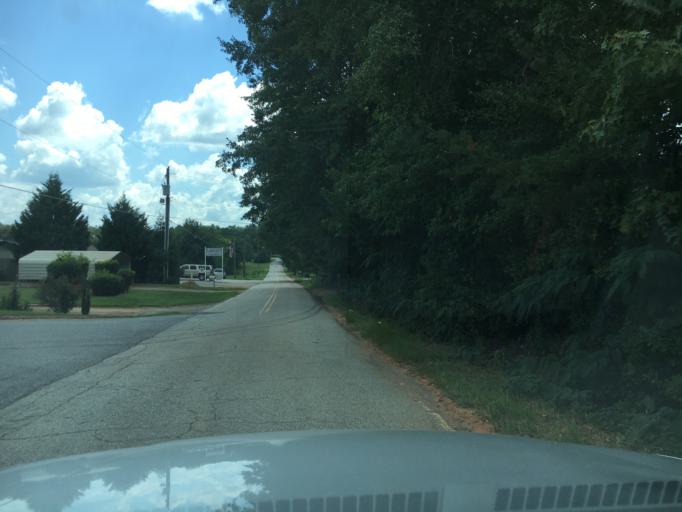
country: US
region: South Carolina
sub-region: Spartanburg County
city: Wellford
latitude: 34.8882
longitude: -82.0591
